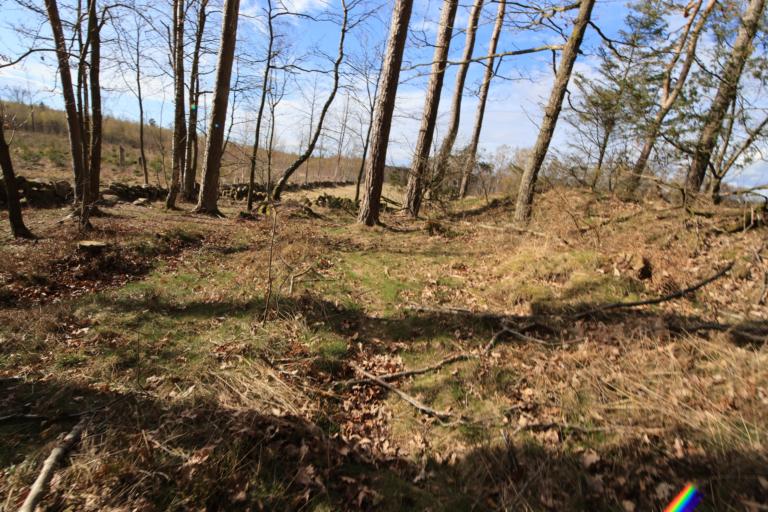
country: SE
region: Halland
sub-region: Varbergs Kommun
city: Varberg
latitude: 57.1728
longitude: 12.2654
